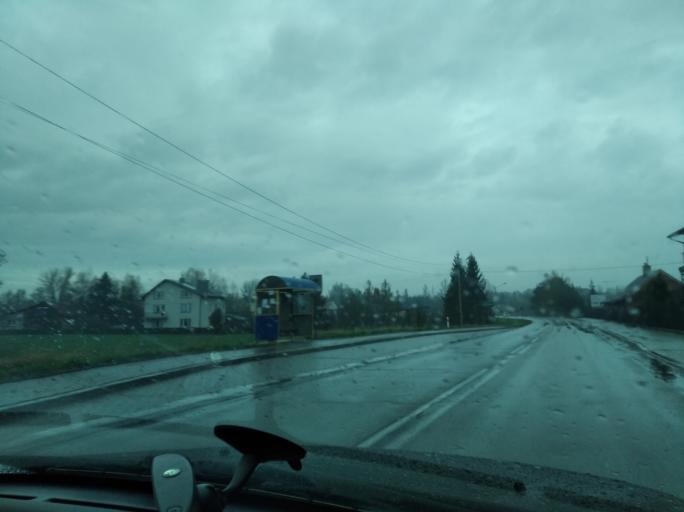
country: PL
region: Subcarpathian Voivodeship
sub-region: Powiat lancucki
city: Albigowa
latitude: 50.0367
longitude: 22.2299
